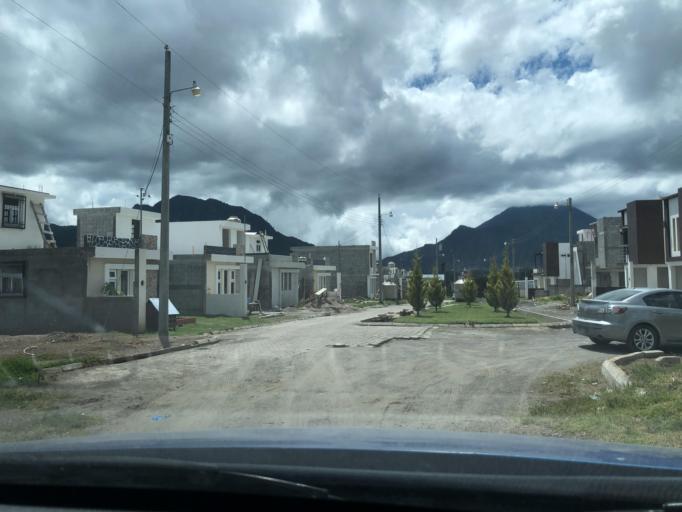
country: GT
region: Quetzaltenango
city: Quetzaltenango
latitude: 14.8404
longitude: -91.5453
